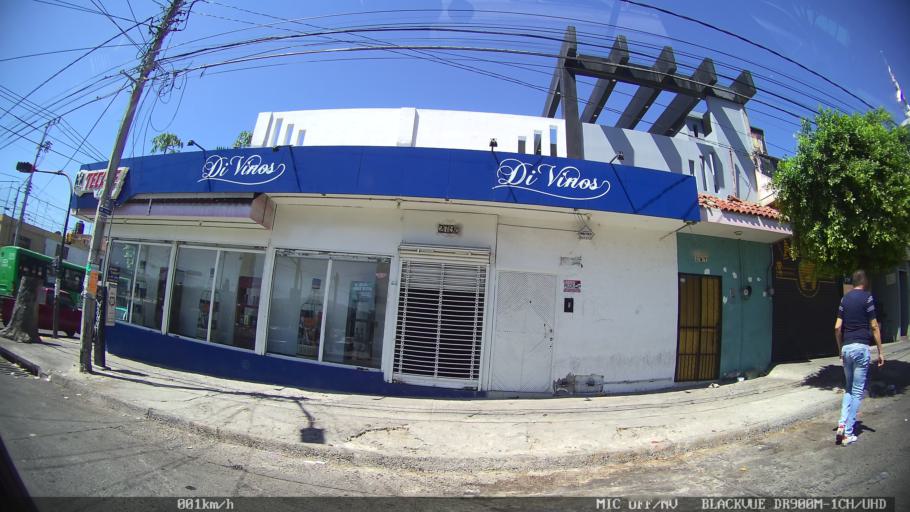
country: MX
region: Jalisco
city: Tlaquepaque
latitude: 20.6973
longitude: -103.2911
